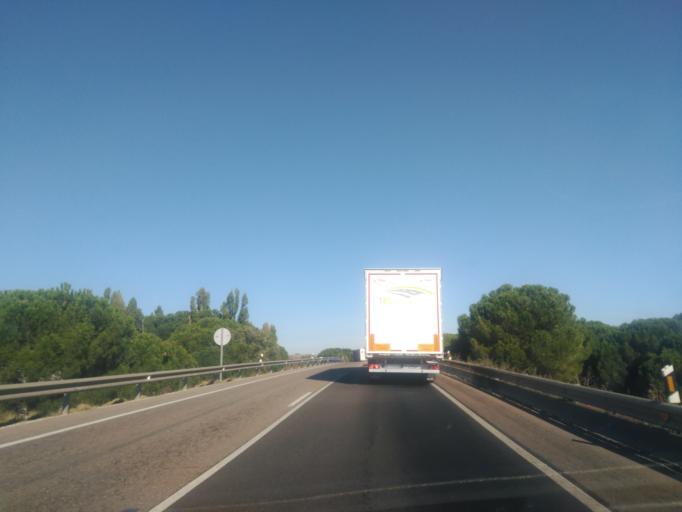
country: ES
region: Castille and Leon
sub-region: Provincia de Valladolid
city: Penafiel
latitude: 41.6057
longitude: -4.1405
